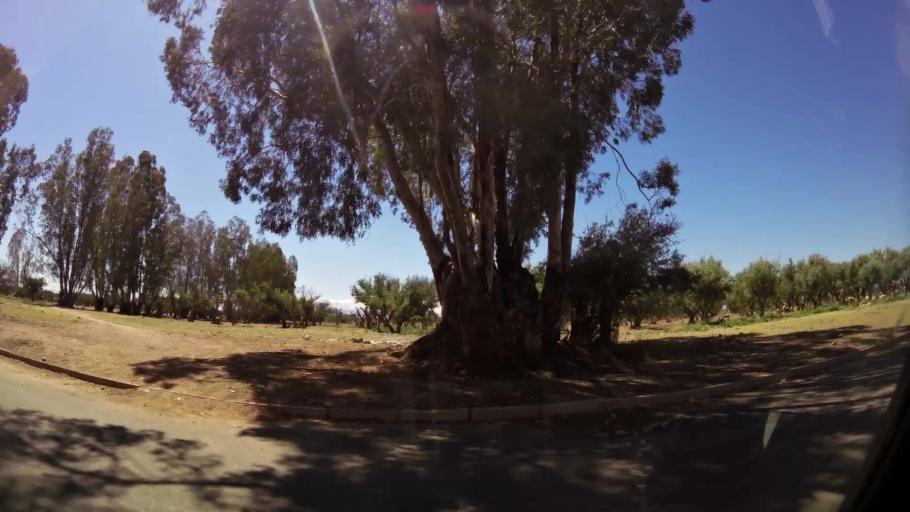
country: MA
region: Marrakech-Tensift-Al Haouz
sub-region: Marrakech
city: Marrakesh
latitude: 31.5697
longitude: -7.9843
